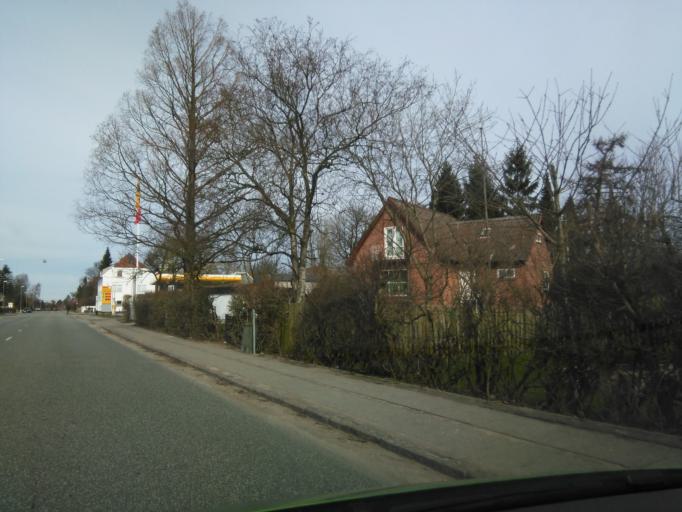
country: DK
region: Central Jutland
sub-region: Arhus Kommune
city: Arhus
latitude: 56.1192
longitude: 10.1929
